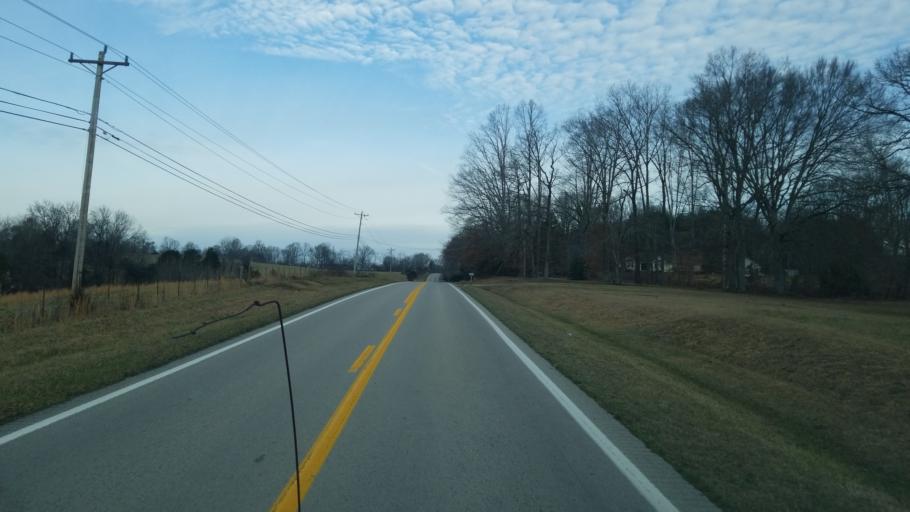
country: US
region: Kentucky
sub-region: Clinton County
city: Albany
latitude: 36.7758
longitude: -85.1729
